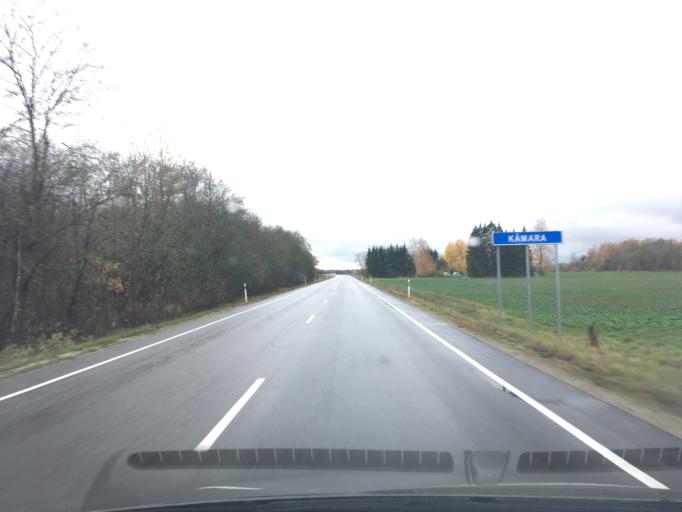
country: EE
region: Jogevamaa
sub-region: Tabivere vald
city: Tabivere
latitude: 58.4614
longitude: 26.5446
